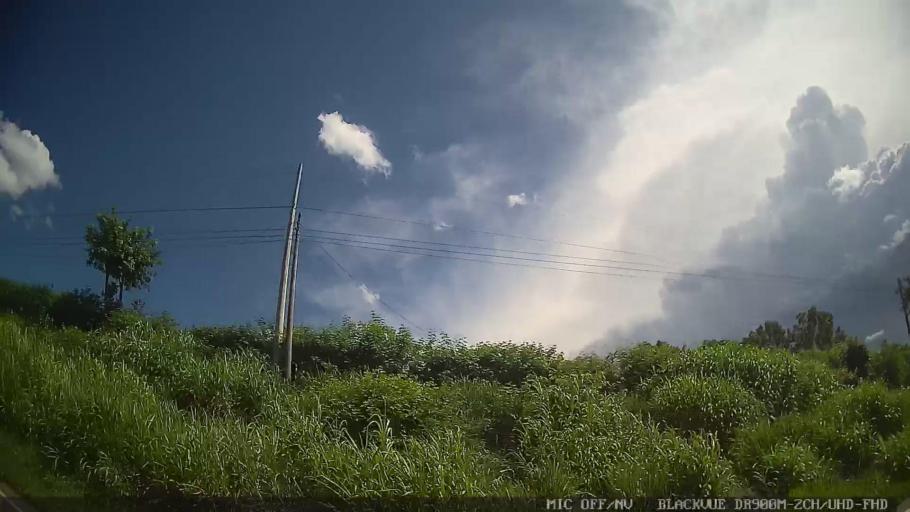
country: BR
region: Sao Paulo
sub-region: Pedreira
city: Pedreira
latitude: -22.7345
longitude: -46.8658
